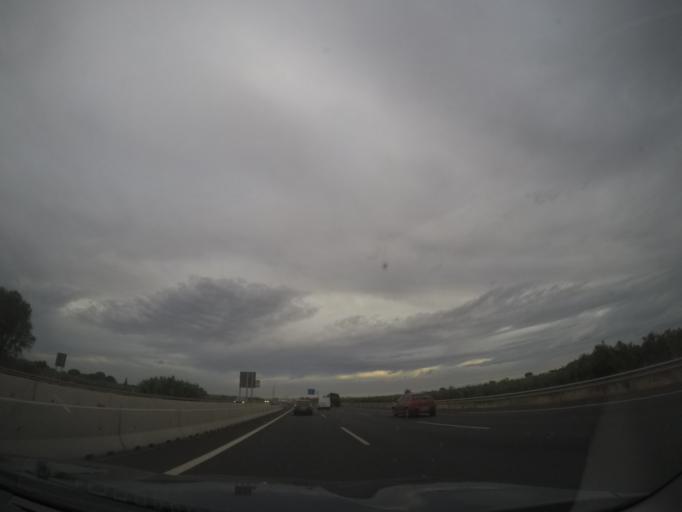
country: ES
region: Andalusia
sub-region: Provincia de Sevilla
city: Benacazon
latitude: 37.3579
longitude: -6.1819
